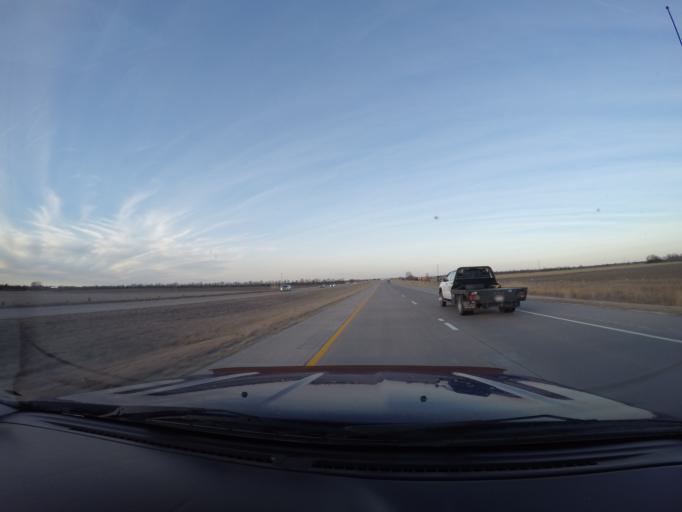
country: US
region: Kansas
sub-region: McPherson County
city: Lindsborg
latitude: 38.6946
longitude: -97.6217
